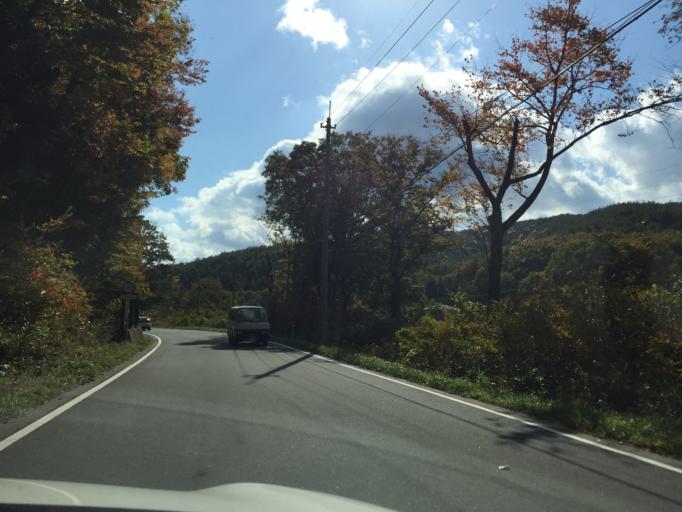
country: JP
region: Fukushima
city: Namie
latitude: 37.3350
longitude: 140.8113
